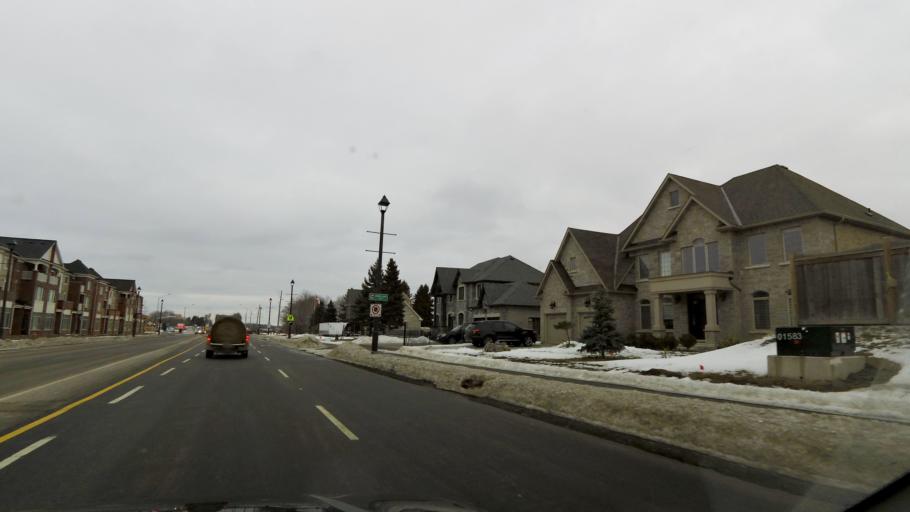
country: CA
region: Ontario
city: Brampton
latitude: 43.8775
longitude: -79.8564
